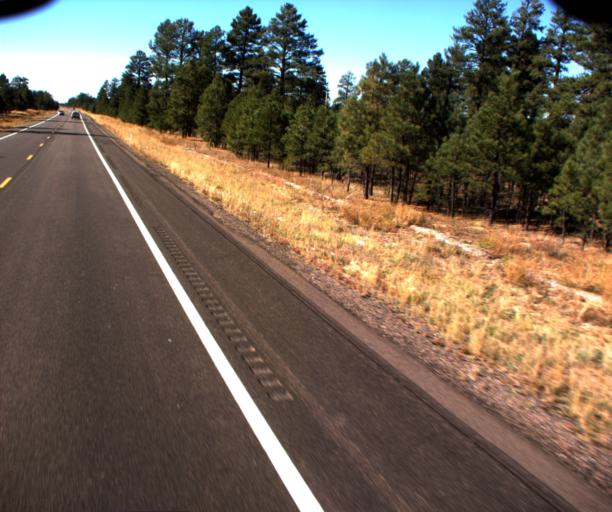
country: US
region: Arizona
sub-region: Apache County
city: Saint Michaels
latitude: 35.6952
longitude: -109.2716
